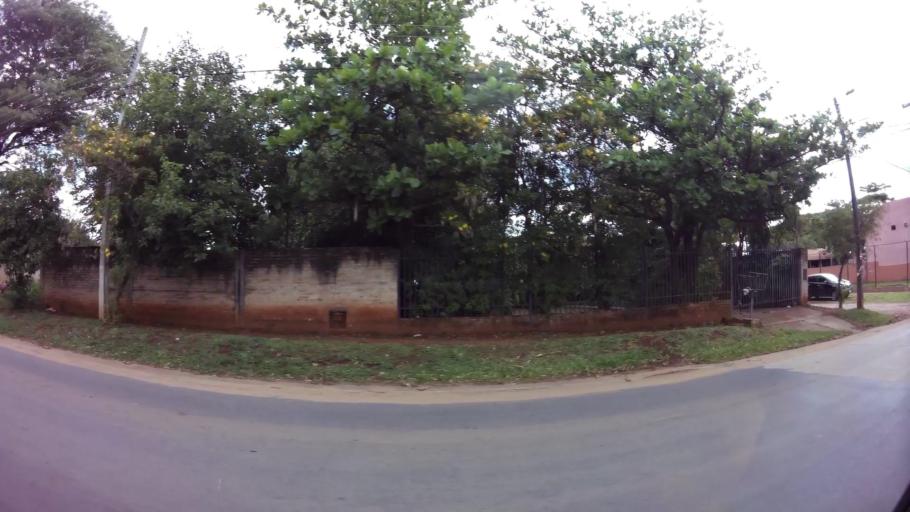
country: PY
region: Central
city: Fernando de la Mora
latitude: -25.2884
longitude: -57.5111
